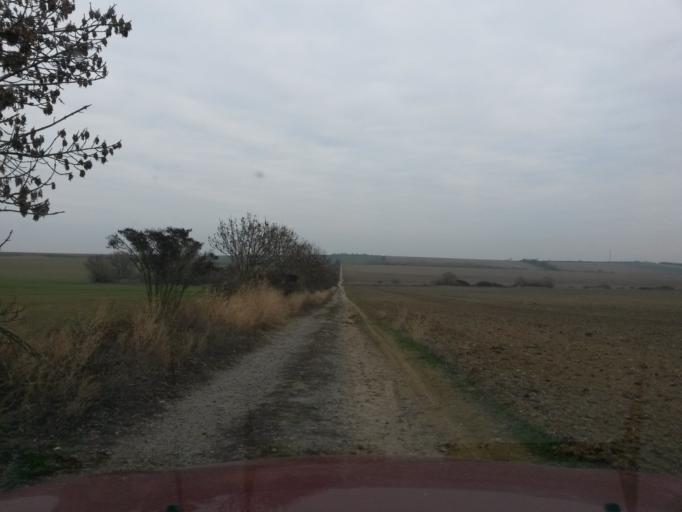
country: SK
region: Kosicky
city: Secovce
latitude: 48.6408
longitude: 21.5902
